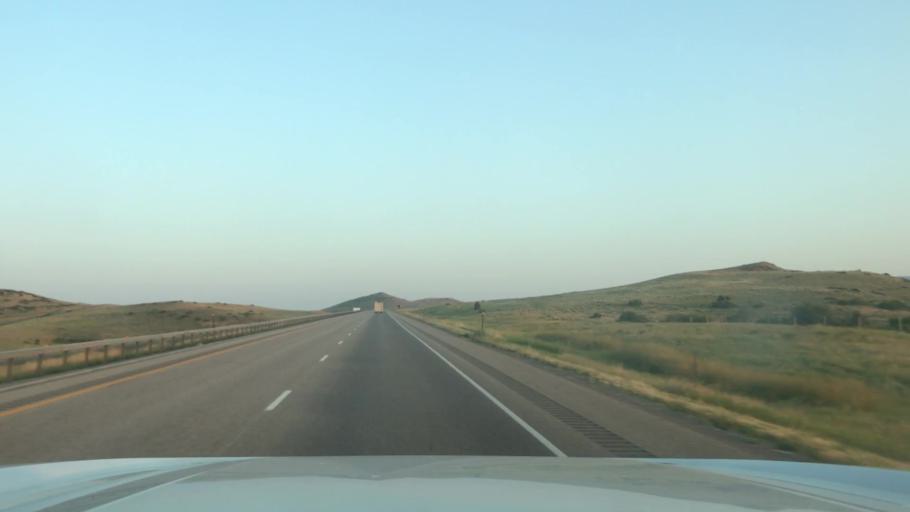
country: US
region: Wyoming
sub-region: Sheridan County
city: Sheridan
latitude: 44.7165
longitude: -106.9147
